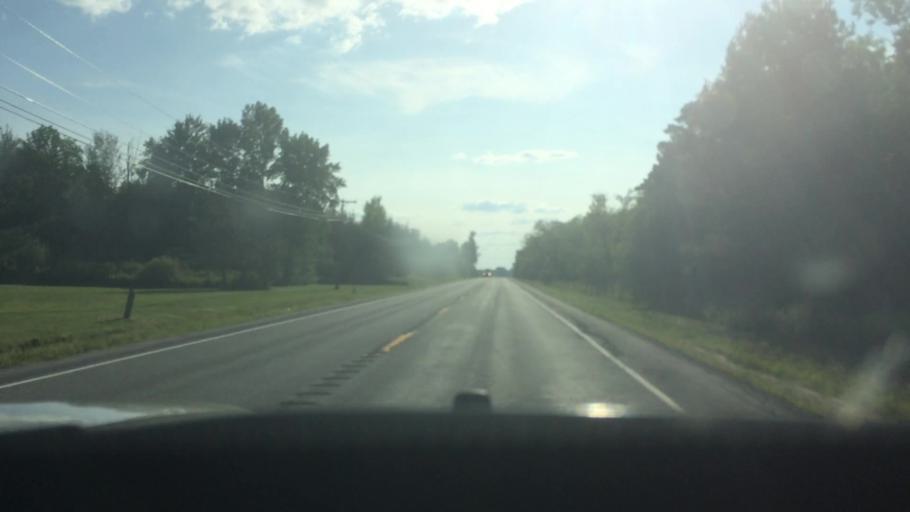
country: US
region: New York
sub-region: St. Lawrence County
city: Potsdam
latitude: 44.6804
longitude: -74.8246
